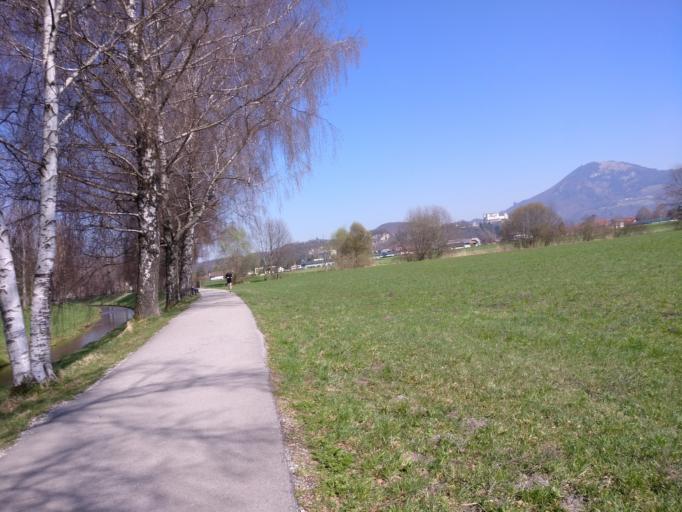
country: AT
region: Salzburg
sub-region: Salzburg Stadt
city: Salzburg
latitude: 47.7857
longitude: 13.0193
